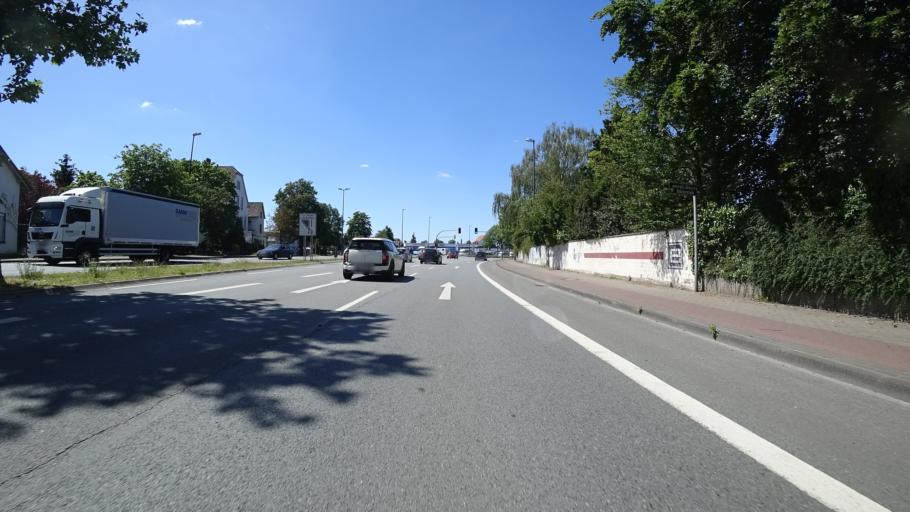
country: DE
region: North Rhine-Westphalia
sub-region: Regierungsbezirk Detmold
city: Guetersloh
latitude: 51.9165
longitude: 8.3926
